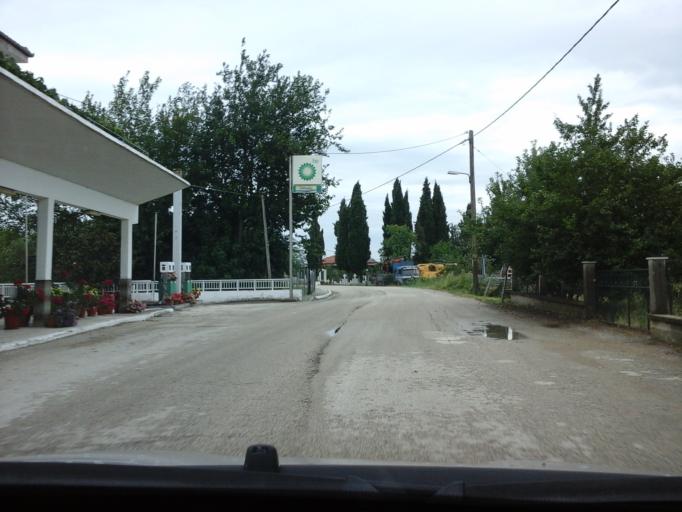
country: GR
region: East Macedonia and Thrace
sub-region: Nomos Evrou
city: Soufli
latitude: 41.1299
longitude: 26.2281
